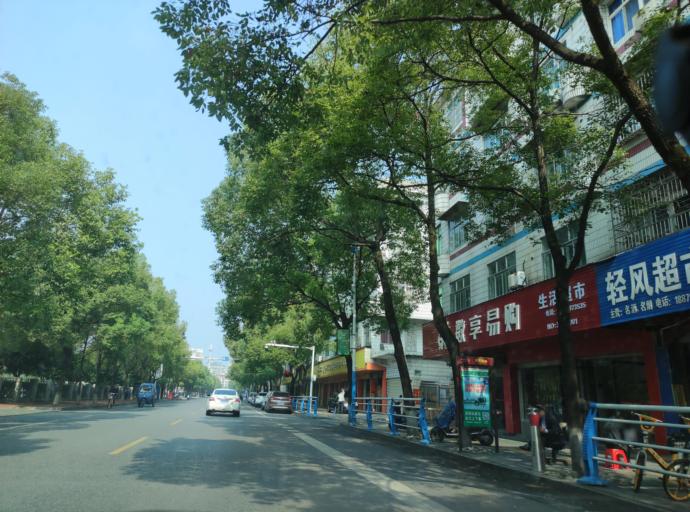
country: CN
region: Jiangxi Sheng
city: Pingxiang
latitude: 27.6427
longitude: 113.8557
